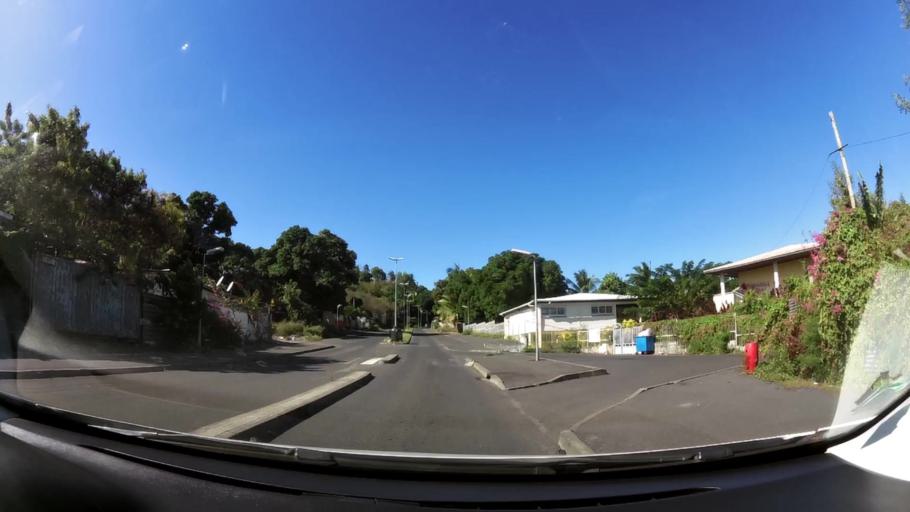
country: YT
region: Pamandzi
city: Pamandzi
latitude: -12.7946
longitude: 45.2740
